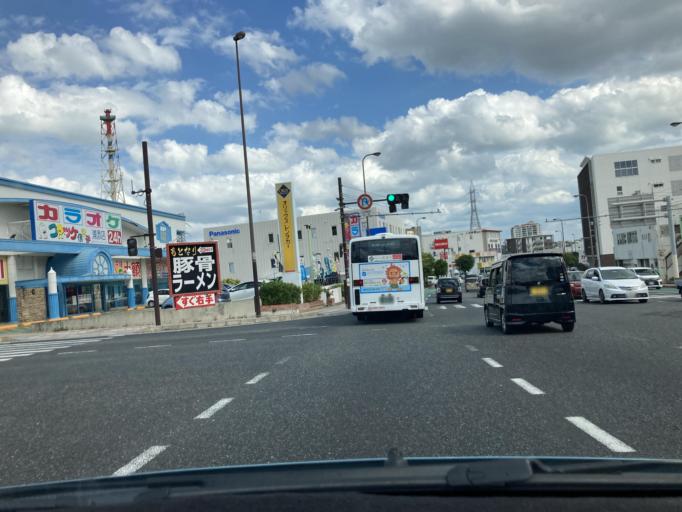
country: JP
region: Okinawa
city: Ginowan
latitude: 26.2674
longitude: 127.7172
